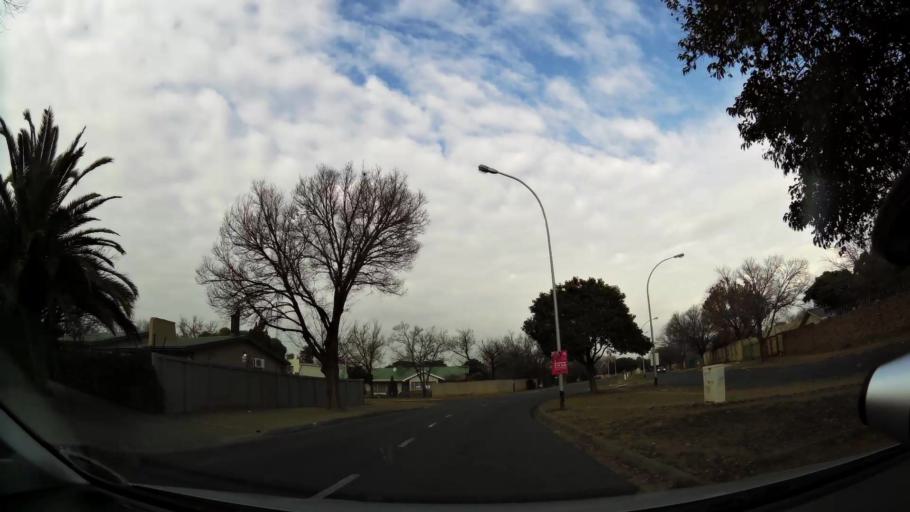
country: ZA
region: Orange Free State
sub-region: Mangaung Metropolitan Municipality
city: Bloemfontein
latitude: -29.1220
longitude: 26.1909
